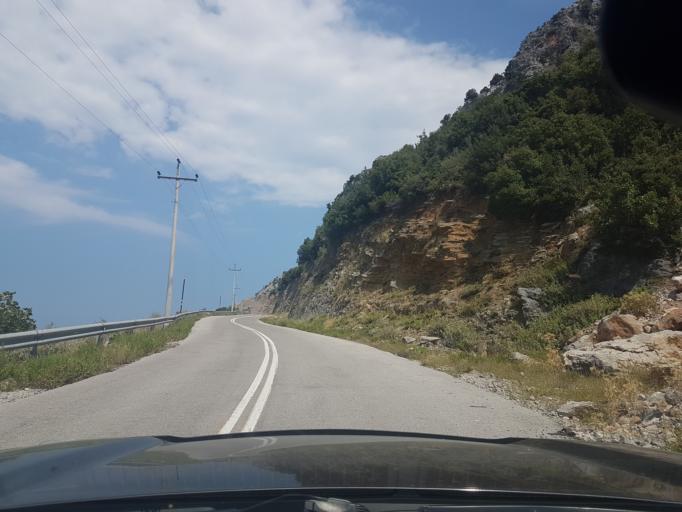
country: GR
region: Central Greece
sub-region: Nomos Evvoias
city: Kymi
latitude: 38.6463
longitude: 23.9623
